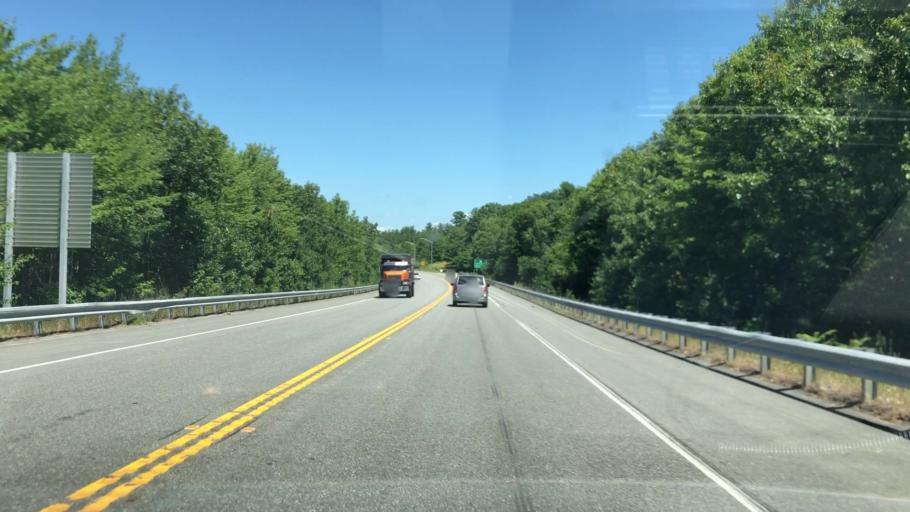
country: US
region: New Hampshire
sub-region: Hillsborough County
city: Milford
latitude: 42.8200
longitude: -71.6246
